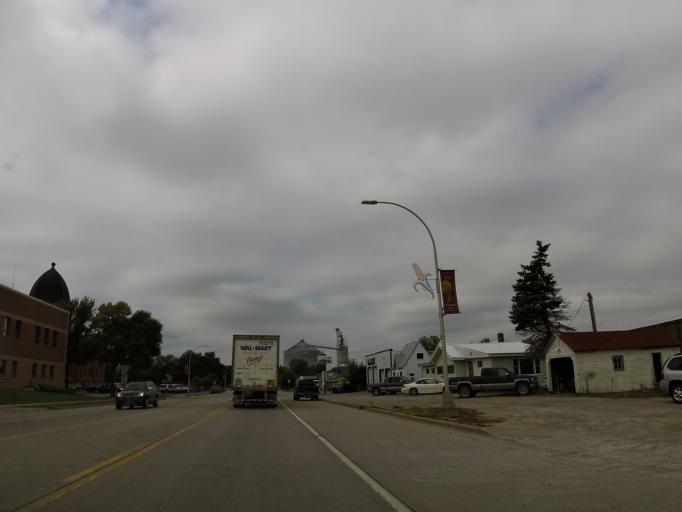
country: US
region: Minnesota
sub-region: Renville County
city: Olivia
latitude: 44.7766
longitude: -94.9815
